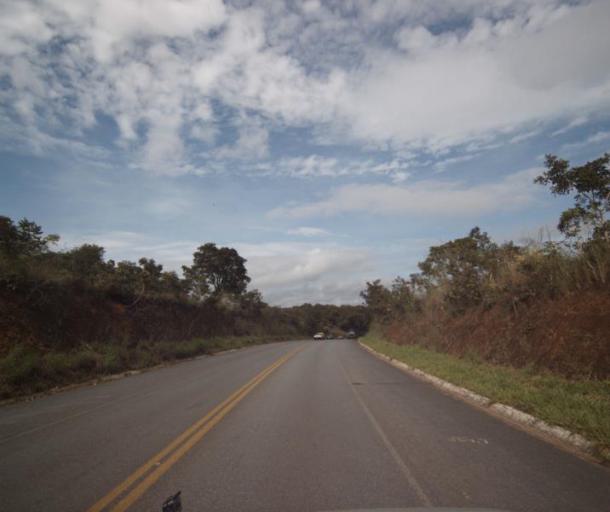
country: BR
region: Goias
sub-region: Pirenopolis
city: Pirenopolis
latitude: -15.6623
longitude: -48.6855
